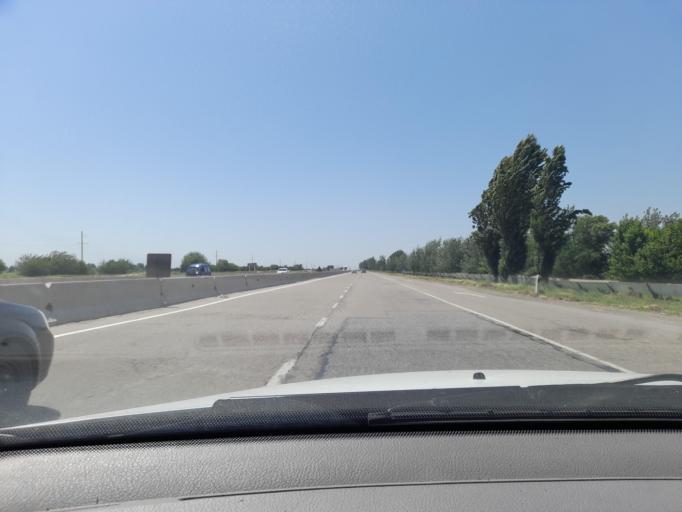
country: UZ
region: Jizzax
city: Dustlik
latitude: 40.4044
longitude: 68.1944
